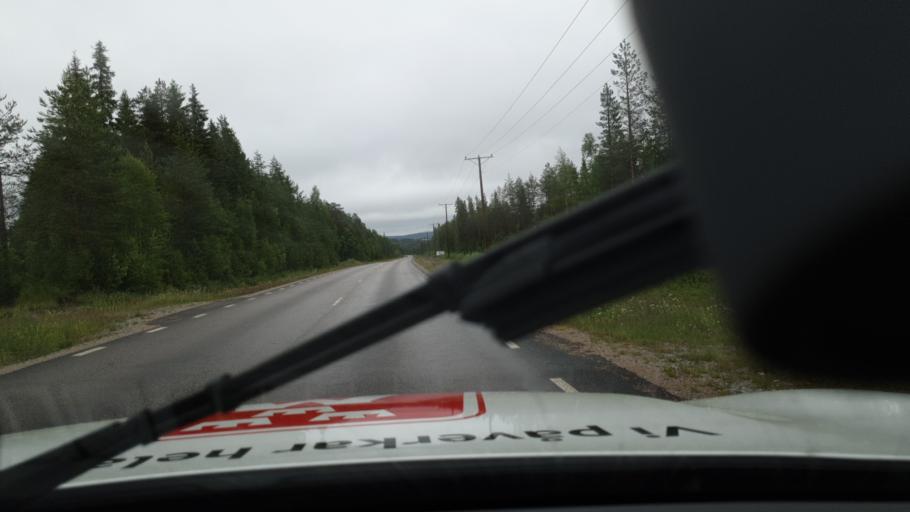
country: SE
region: Norrbotten
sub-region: Overtornea Kommun
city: OEvertornea
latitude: 66.3981
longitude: 23.5768
